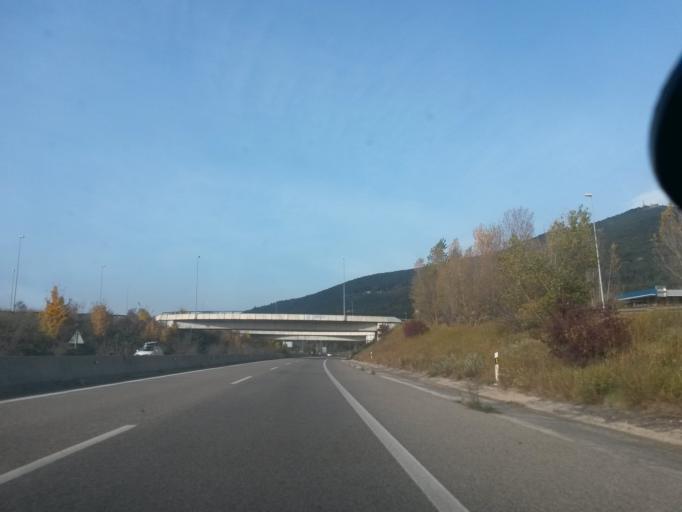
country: ES
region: Catalonia
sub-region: Provincia de Girona
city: Argelaguer
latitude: 42.2195
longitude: 2.5834
